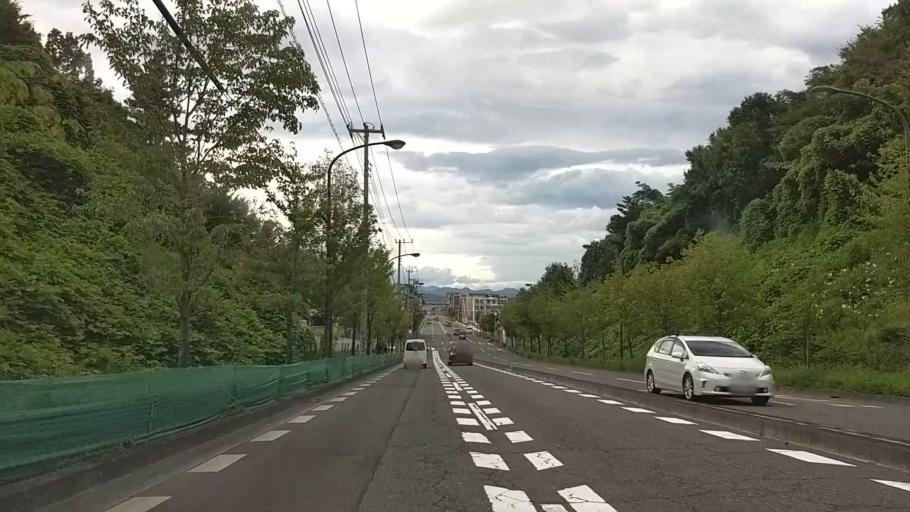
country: JP
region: Tokyo
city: Hachioji
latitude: 35.6319
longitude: 139.3352
